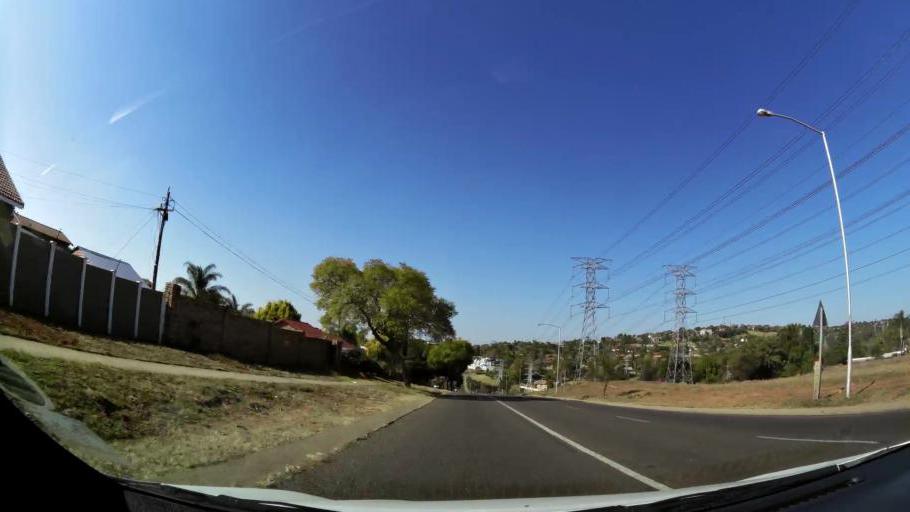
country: ZA
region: Gauteng
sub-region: City of Tshwane Metropolitan Municipality
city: Centurion
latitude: -25.8210
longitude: 28.2747
